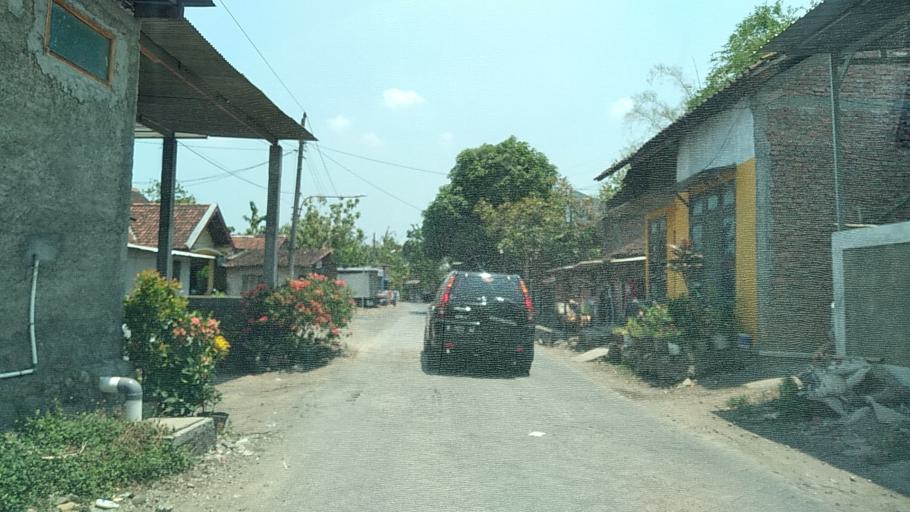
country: ID
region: Central Java
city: Mranggen
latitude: -7.0068
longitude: 110.4882
